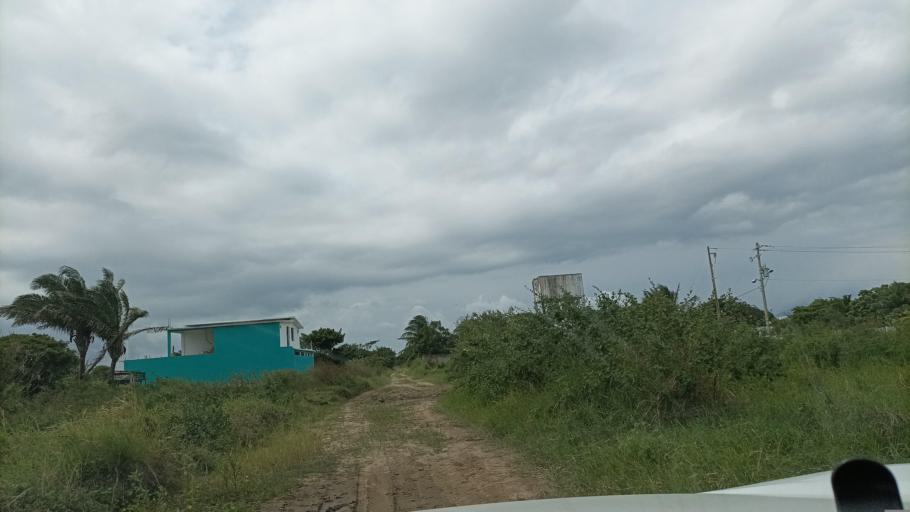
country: MX
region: Veracruz
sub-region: Coatzacoalcos
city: Fraccionamiento Ciudad Olmeca
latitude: 18.1786
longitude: -94.5921
